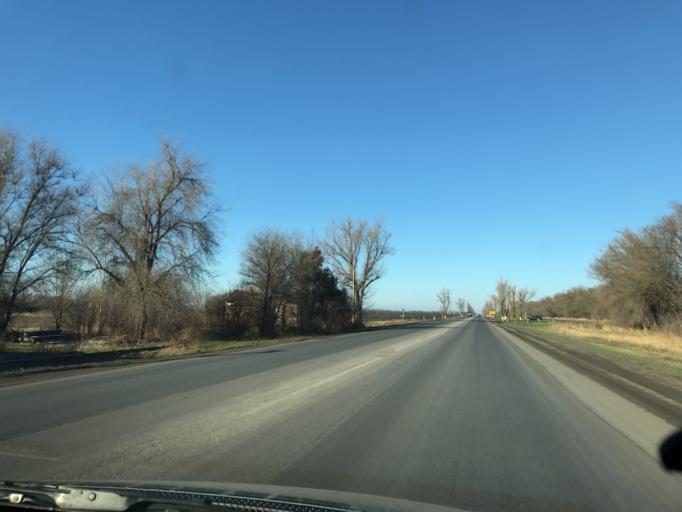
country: RU
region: Rostov
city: Zernograd
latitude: 46.8339
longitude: 40.2341
